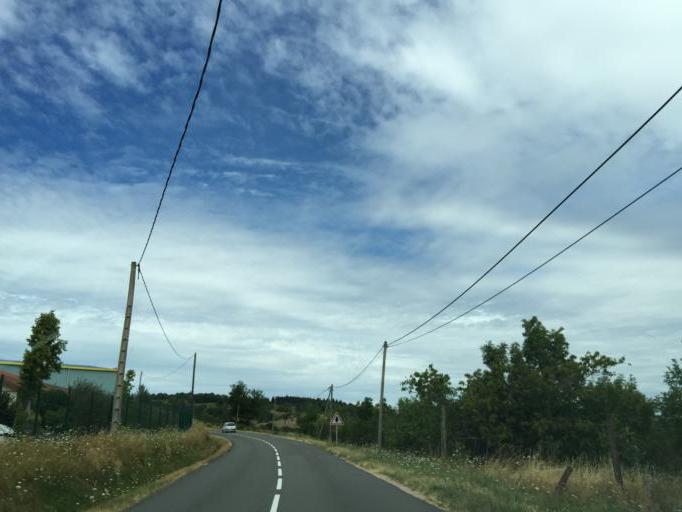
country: FR
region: Rhone-Alpes
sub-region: Departement de la Loire
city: Saint-Bonnet-le-Chateau
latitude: 45.4133
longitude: 4.0934
